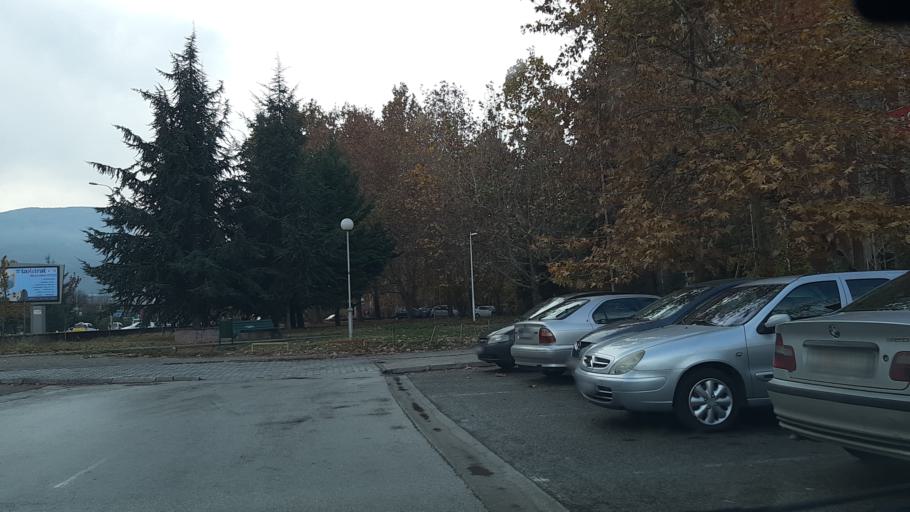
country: MK
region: Karpos
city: Skopje
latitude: 41.9891
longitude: 21.4558
